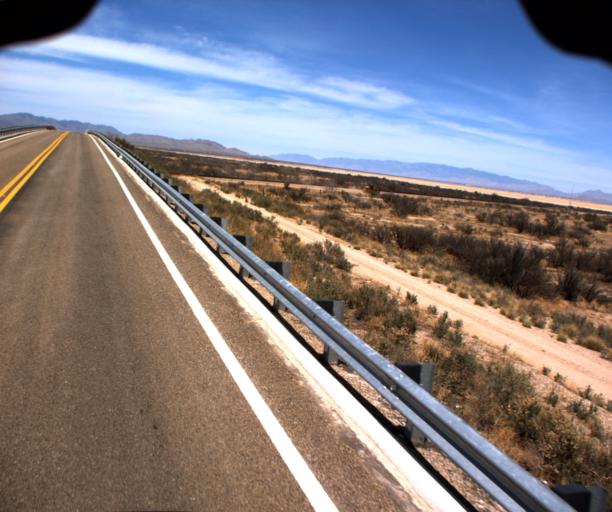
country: US
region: Arizona
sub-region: Cochise County
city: Willcox
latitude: 32.1324
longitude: -109.9100
